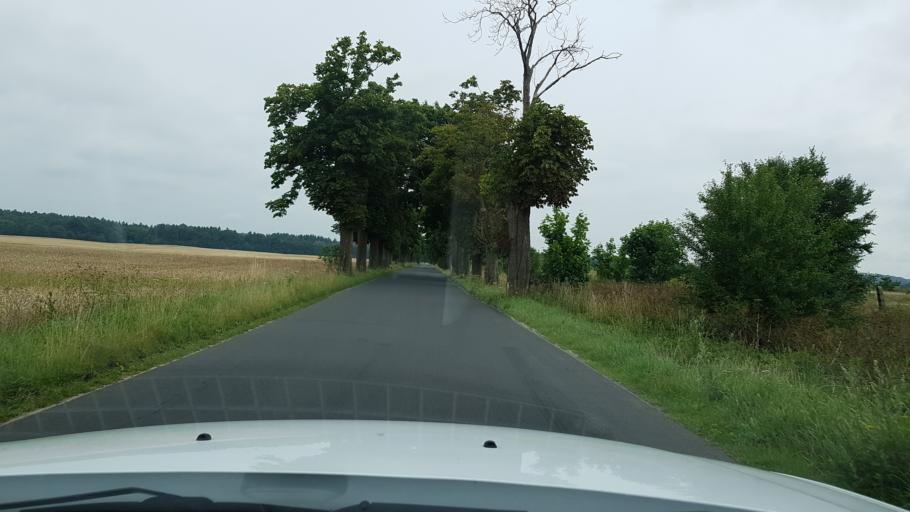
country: PL
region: West Pomeranian Voivodeship
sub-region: Powiat slawienski
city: Slawno
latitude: 54.5041
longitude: 16.5734
